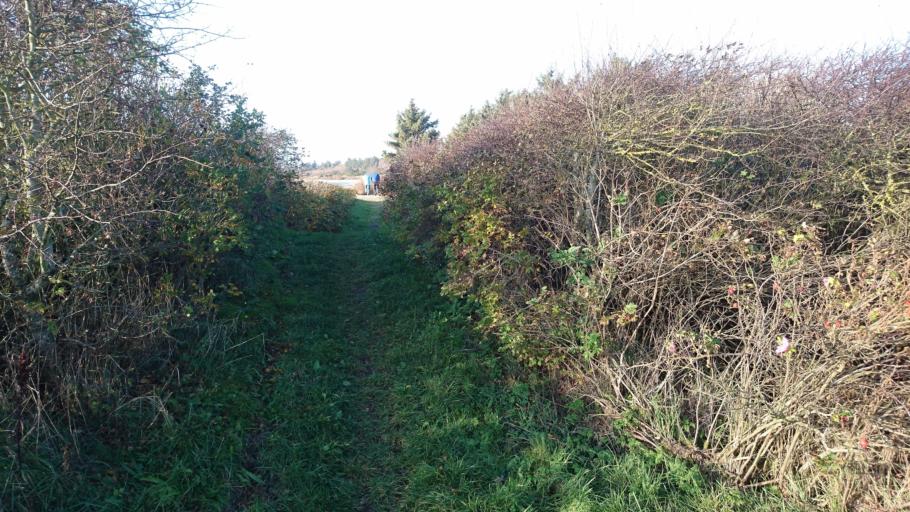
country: DK
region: North Denmark
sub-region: Morso Kommune
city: Nykobing Mors
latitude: 56.8272
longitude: 8.9662
